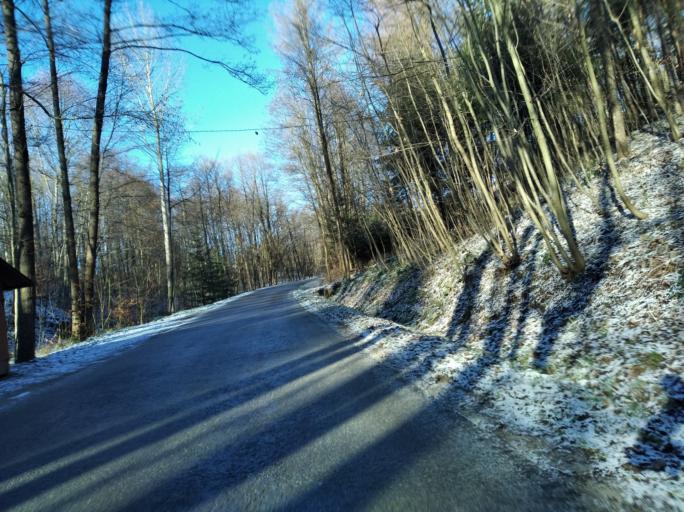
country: PL
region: Subcarpathian Voivodeship
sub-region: Powiat ropczycko-sedziszowski
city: Iwierzyce
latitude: 49.9647
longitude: 21.7553
